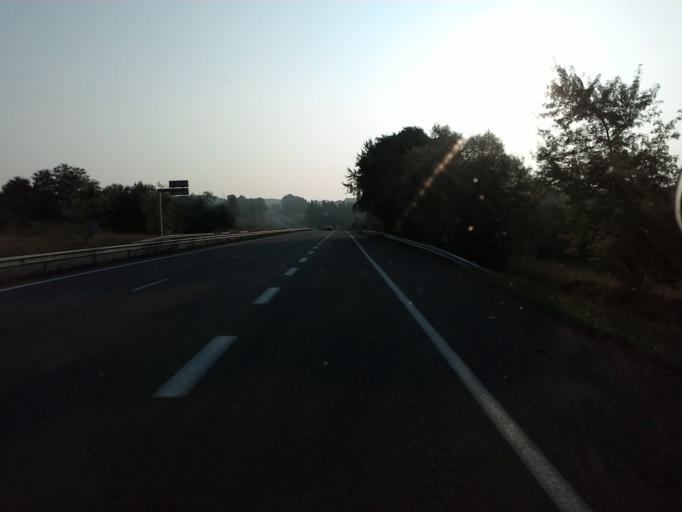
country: FR
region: Franche-Comte
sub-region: Departement du Doubs
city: Devecey
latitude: 47.3476
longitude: 6.0187
